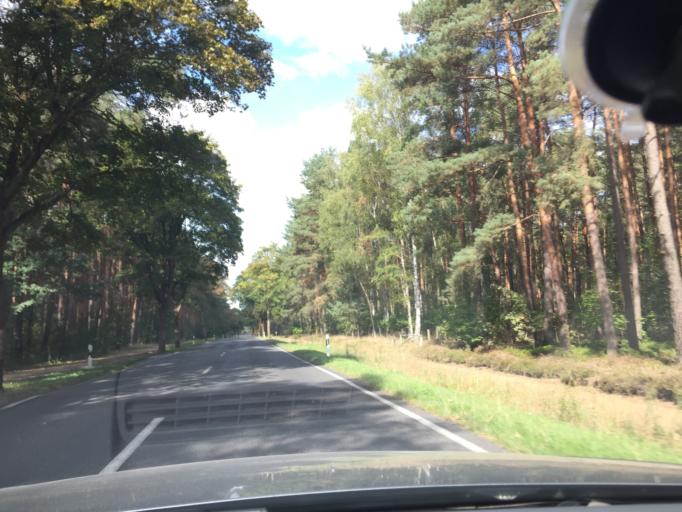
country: DE
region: Brandenburg
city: Grunheide
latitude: 52.3869
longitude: 13.8283
